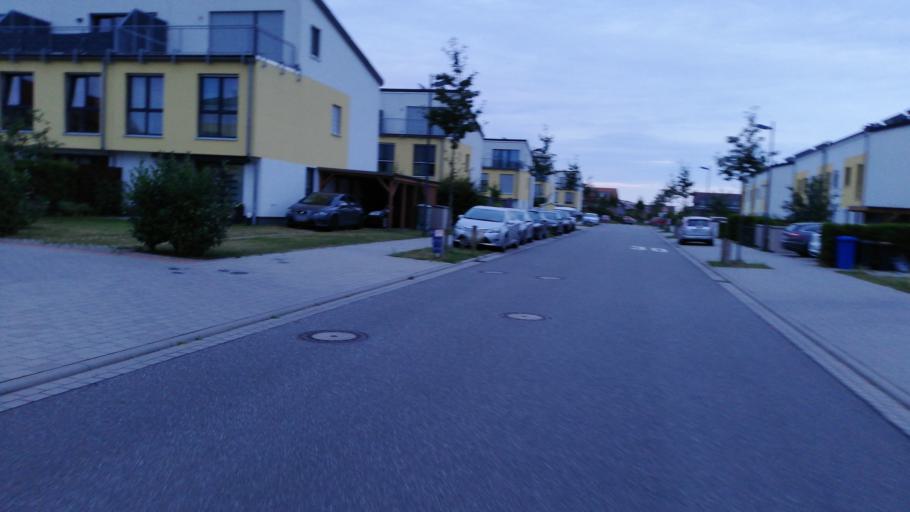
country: DE
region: Lower Saxony
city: Neu Wulmstorf
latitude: 53.4762
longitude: 9.7917
